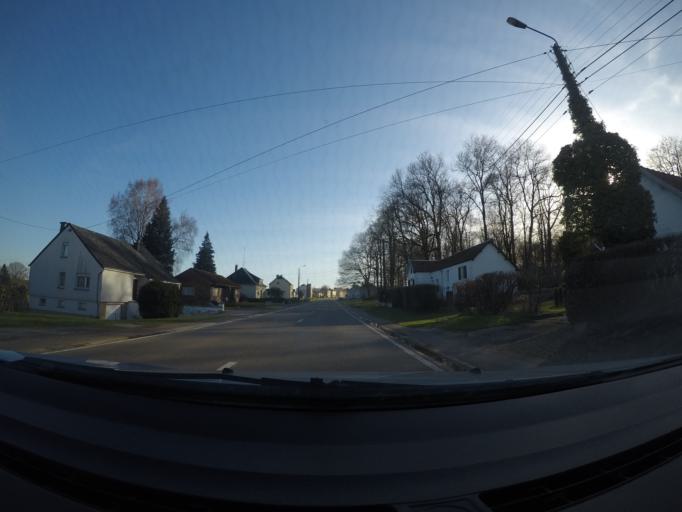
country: BE
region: Wallonia
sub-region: Province du Luxembourg
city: Tintigny
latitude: 49.6690
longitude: 5.5015
